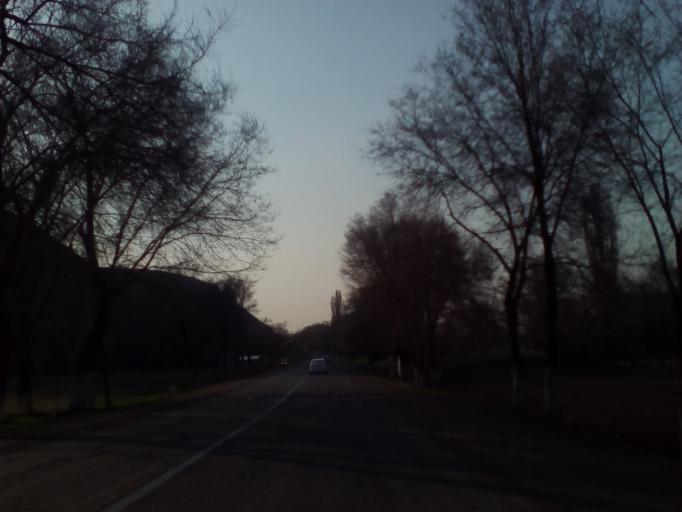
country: KZ
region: Almaty Oblysy
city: Burunday
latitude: 43.1673
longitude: 76.5430
